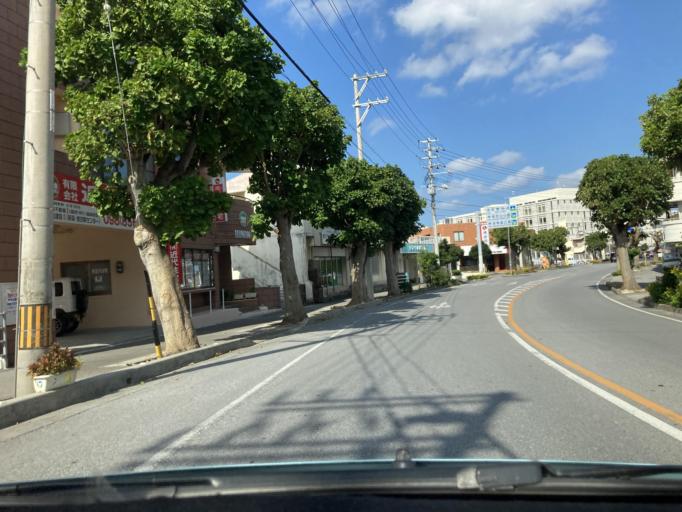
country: JP
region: Okinawa
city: Tomigusuku
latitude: 26.1755
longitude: 127.6831
